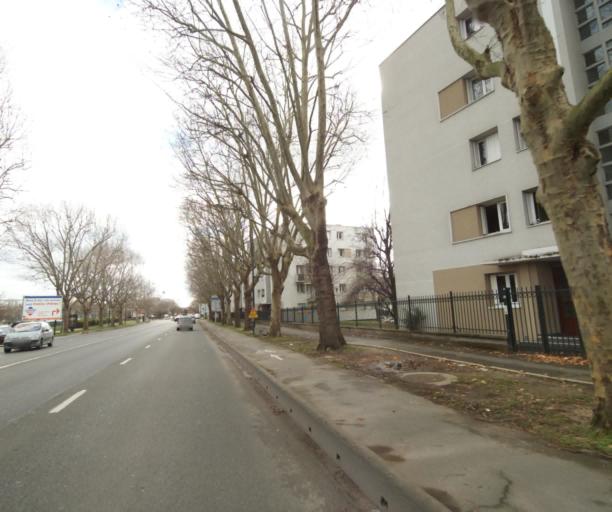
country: FR
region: Ile-de-France
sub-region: Departement de Seine-Saint-Denis
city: Saint-Denis
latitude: 48.9409
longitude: 2.3669
